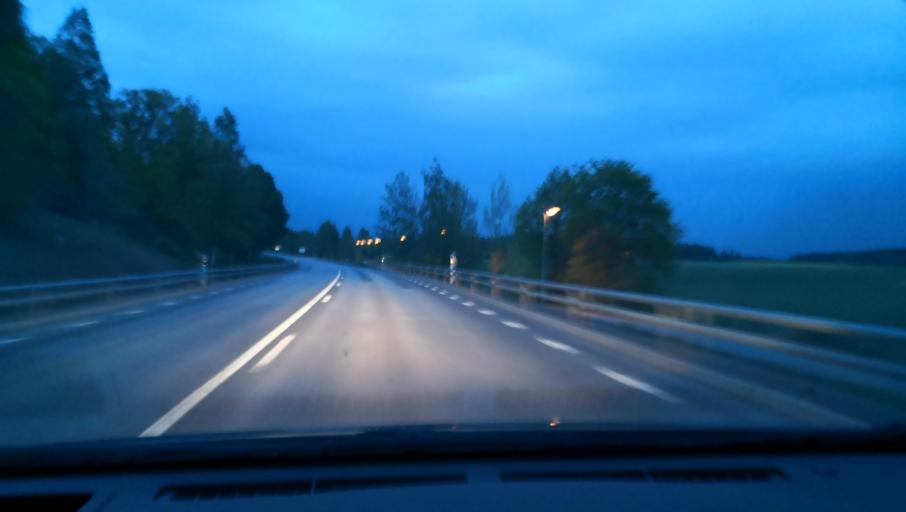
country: SE
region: Vaestmanland
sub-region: Kopings Kommun
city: Kolsva
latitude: 59.5542
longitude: 15.9003
